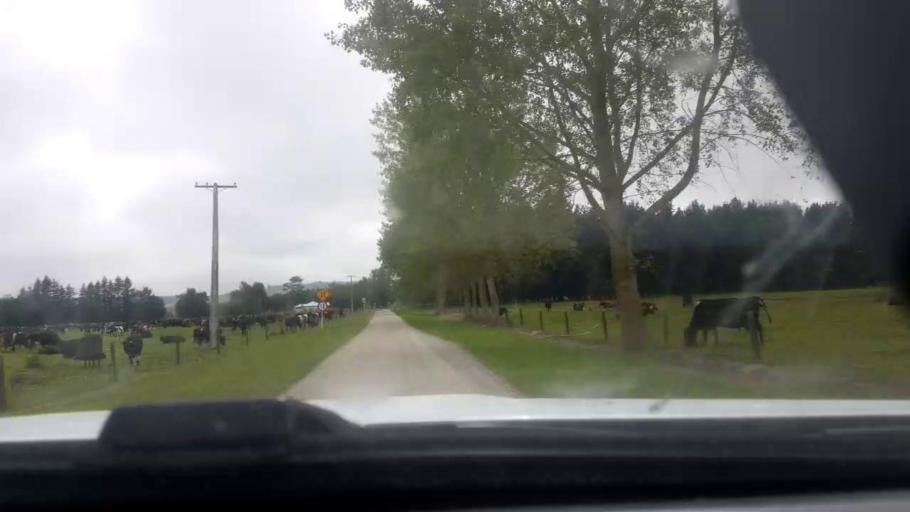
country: NZ
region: Canterbury
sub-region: Timaru District
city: Pleasant Point
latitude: -44.2094
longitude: 171.1116
